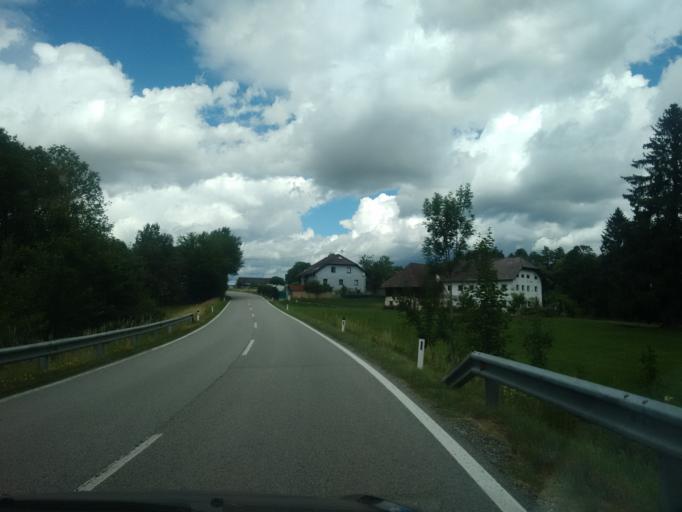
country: AT
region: Upper Austria
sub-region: Politischer Bezirk Urfahr-Umgebung
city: Gramastetten
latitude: 48.4179
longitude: 14.1623
